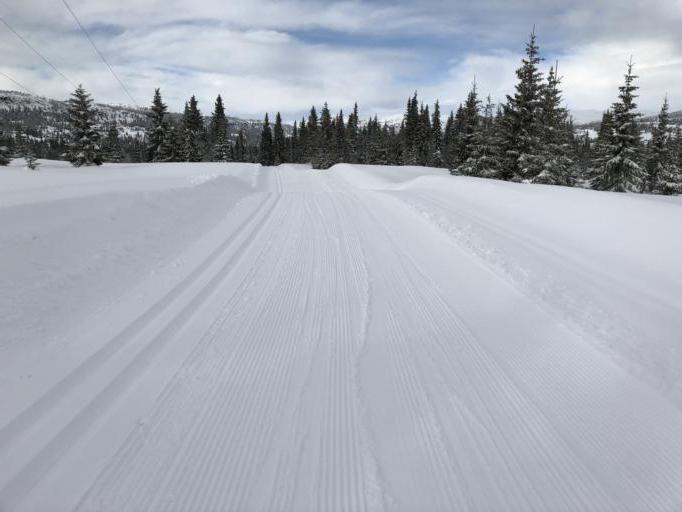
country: NO
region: Oppland
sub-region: Gausdal
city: Segalstad bru
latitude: 61.3229
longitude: 10.0806
